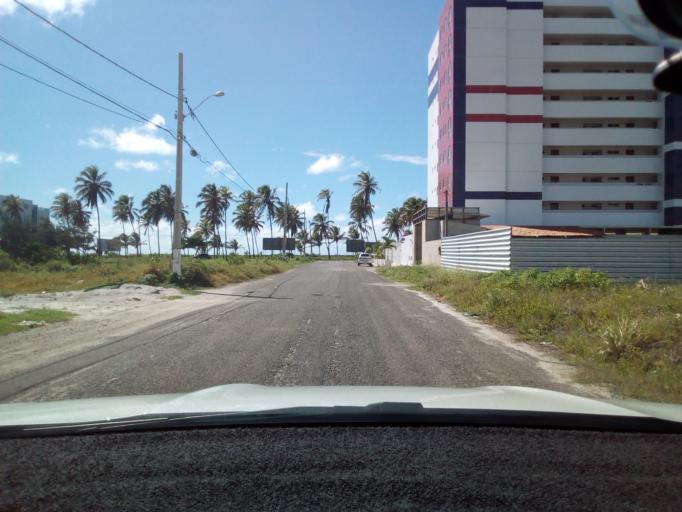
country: BR
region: Paraiba
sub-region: Joao Pessoa
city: Joao Pessoa
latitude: -7.0541
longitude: -34.8448
